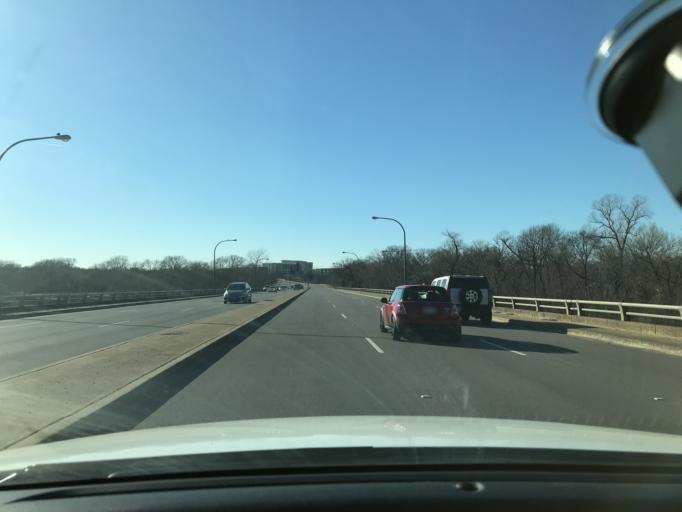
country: US
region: Texas
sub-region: Dallas County
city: Highland Park
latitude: 32.8527
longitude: -96.7217
